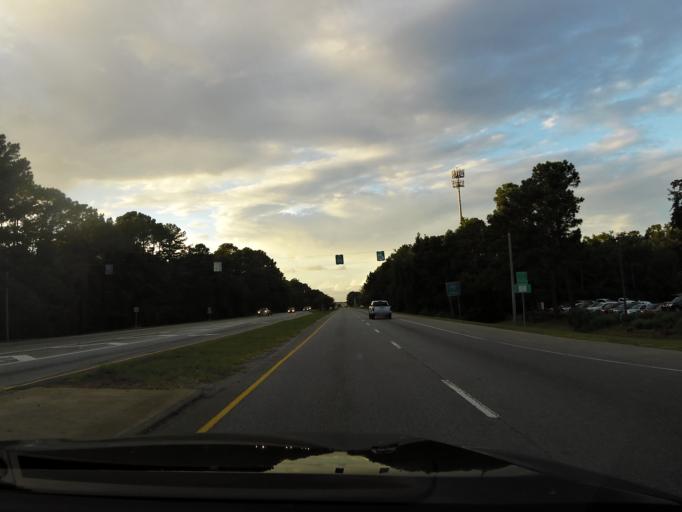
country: US
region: Georgia
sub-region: Glynn County
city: Dock Junction
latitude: 31.2261
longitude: -81.4962
